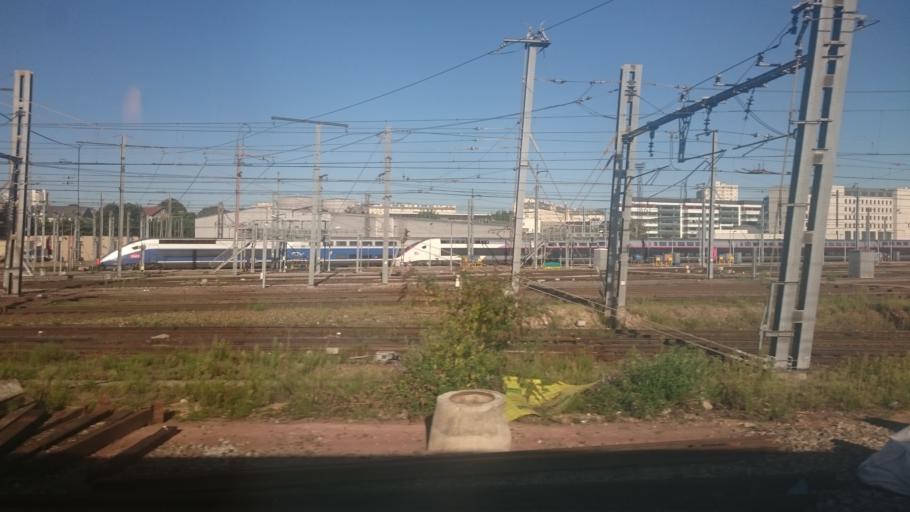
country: FR
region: Ile-de-France
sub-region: Departement des Hauts-de-Seine
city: Chatillon
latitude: 48.8034
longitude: 2.3009
